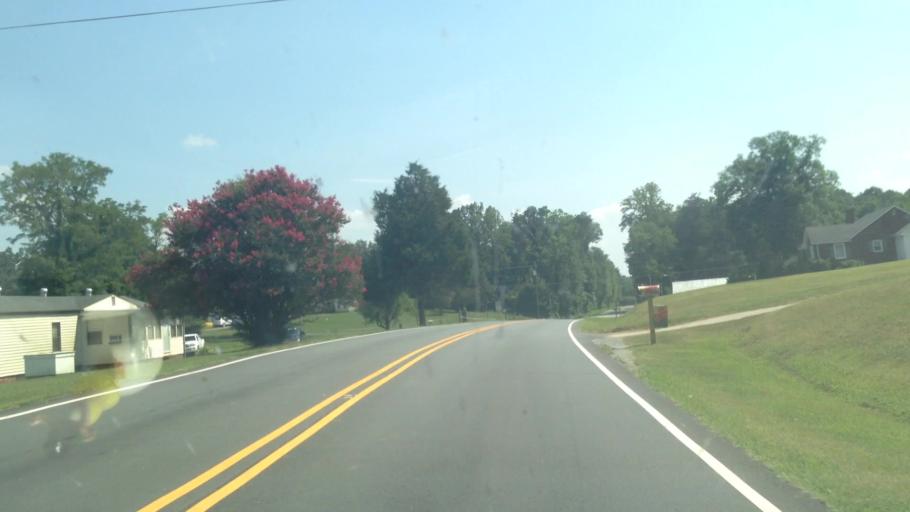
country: US
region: North Carolina
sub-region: Stokes County
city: Danbury
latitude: 36.4036
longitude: -80.0932
